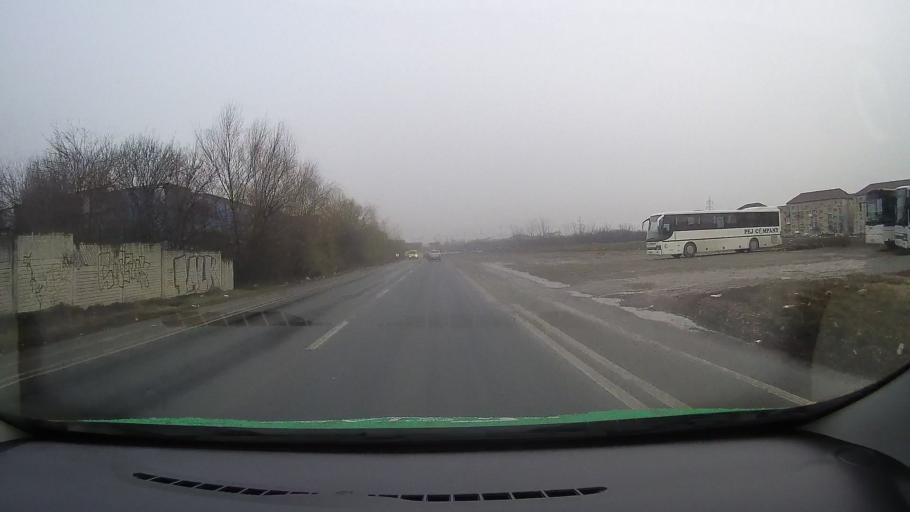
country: RO
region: Timis
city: Timisoara
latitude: 45.7387
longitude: 21.2501
